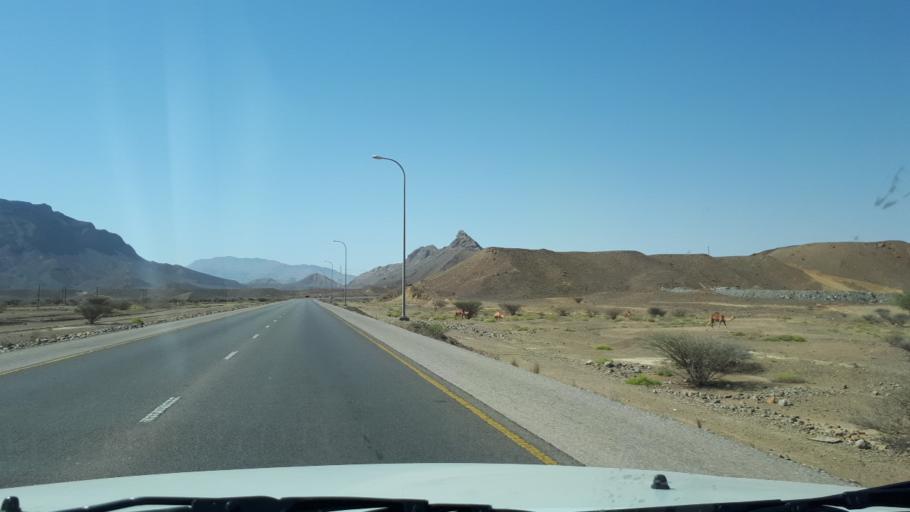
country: OM
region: Ash Sharqiyah
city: Sur
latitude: 22.3460
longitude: 59.3138
